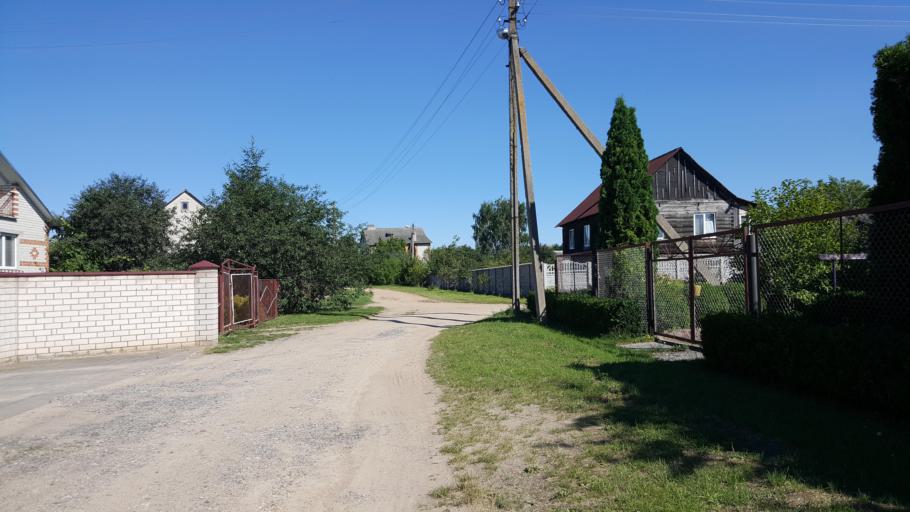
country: BY
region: Brest
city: Charnawchytsy
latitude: 52.2082
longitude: 23.7386
